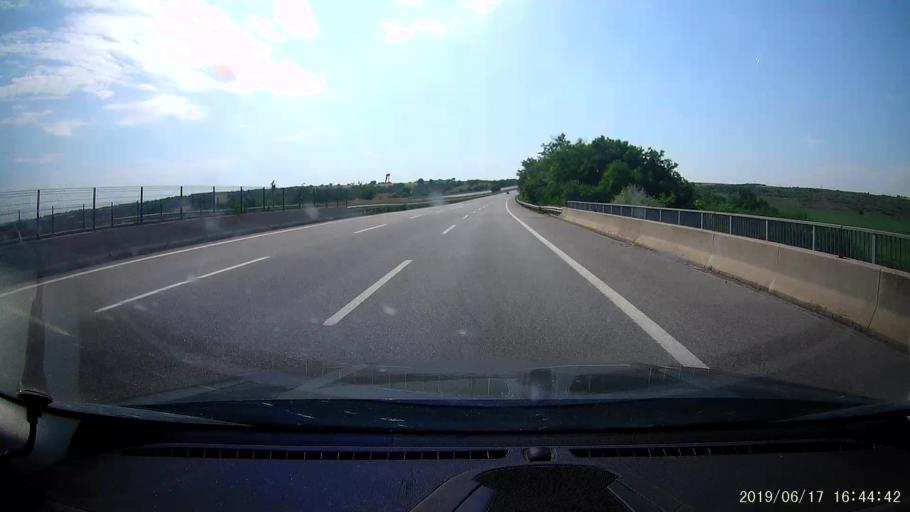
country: TR
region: Kirklareli
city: Luleburgaz
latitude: 41.4821
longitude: 27.2533
